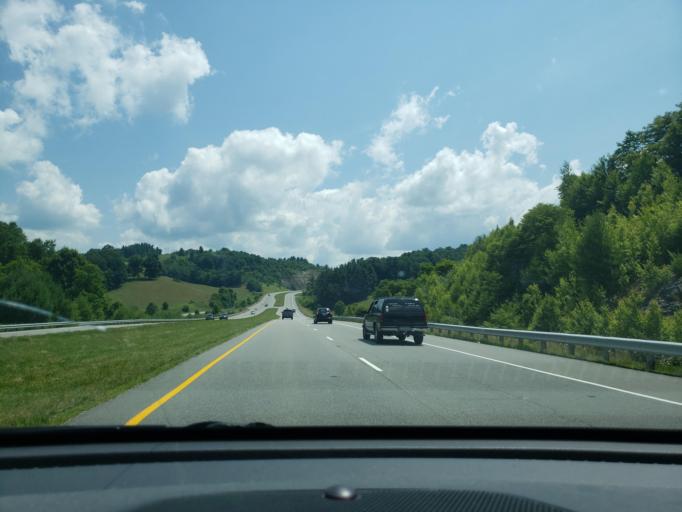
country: US
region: North Carolina
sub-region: Watauga County
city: Boone
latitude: 36.2285
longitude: -81.6002
